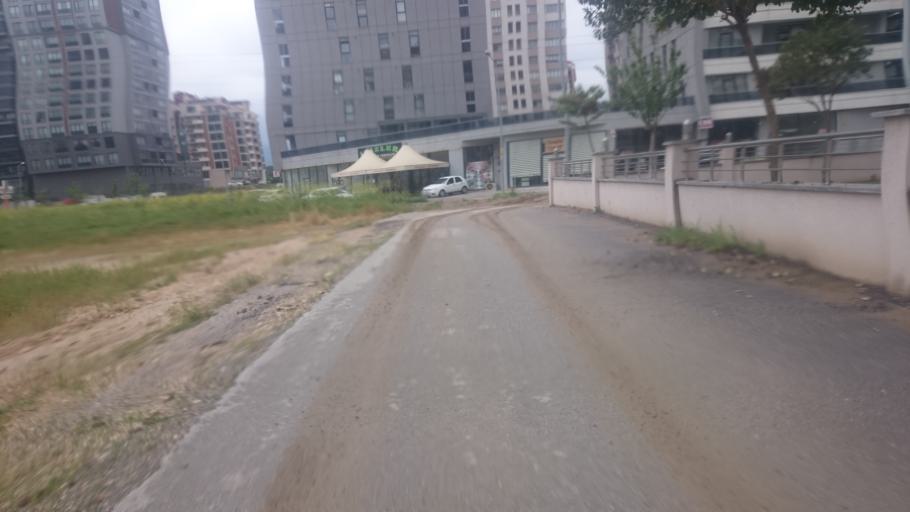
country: TR
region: Bursa
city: Cali
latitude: 40.2190
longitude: 28.9430
